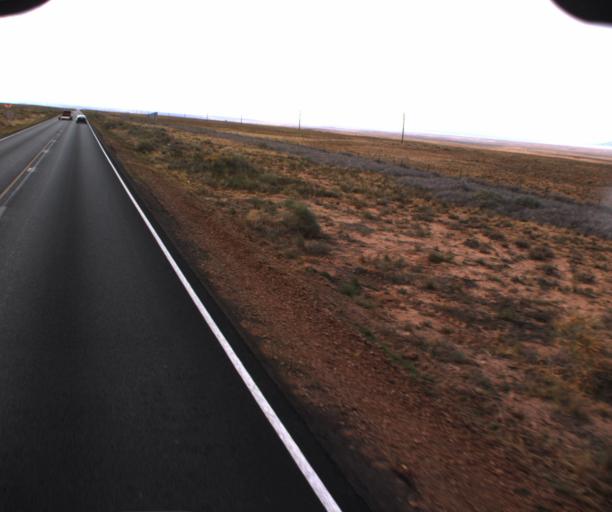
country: US
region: Arizona
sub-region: Apache County
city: Chinle
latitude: 36.0450
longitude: -109.6077
